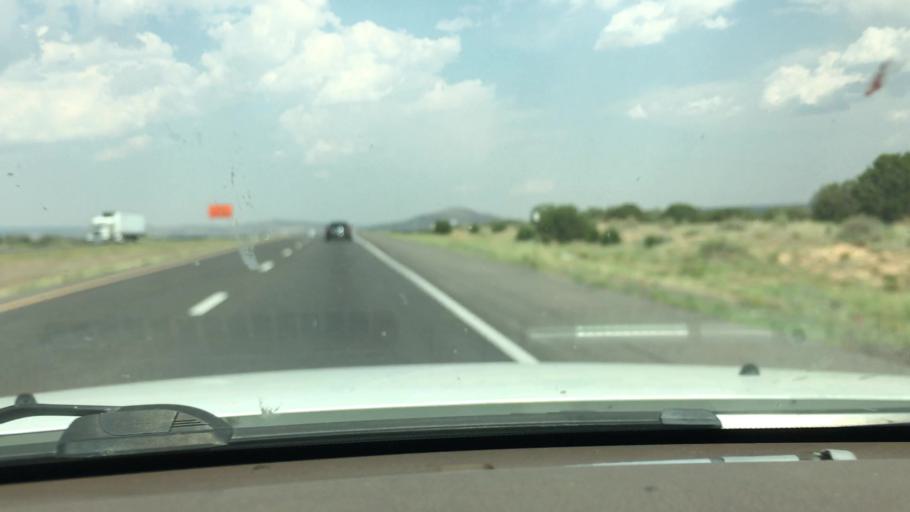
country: US
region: New Mexico
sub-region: Cibola County
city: Skyline-Ganipa
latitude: 35.0752
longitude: -107.6343
